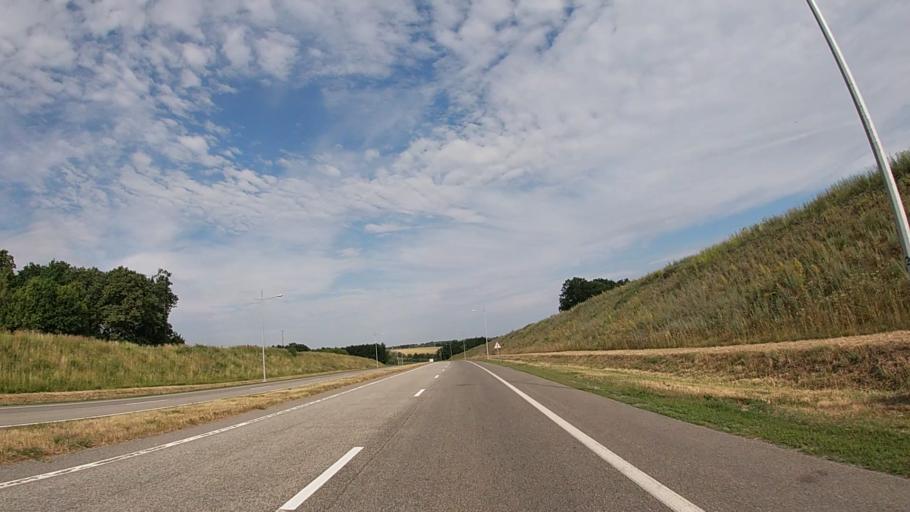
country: RU
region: Belgorod
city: Tomarovka
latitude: 50.7063
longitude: 36.2124
